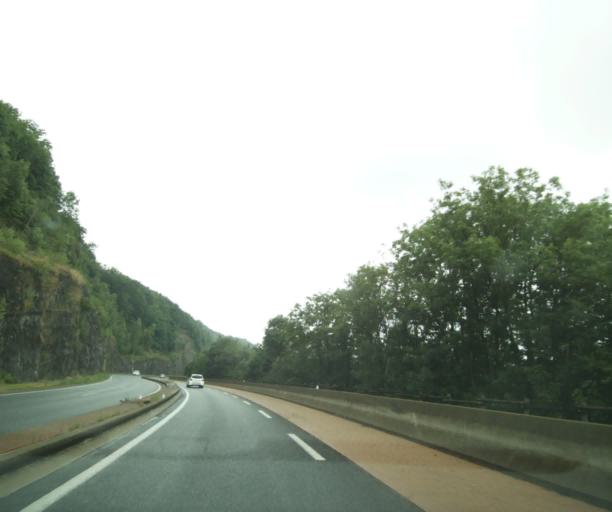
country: FR
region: Midi-Pyrenees
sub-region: Departement de l'Aveyron
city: Olemps
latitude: 44.3465
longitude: 2.5584
